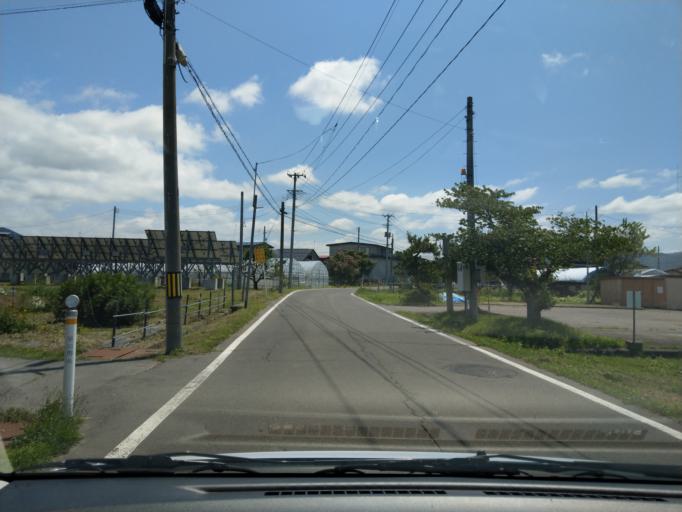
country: JP
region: Aomori
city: Kuroishi
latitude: 40.5760
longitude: 140.5519
